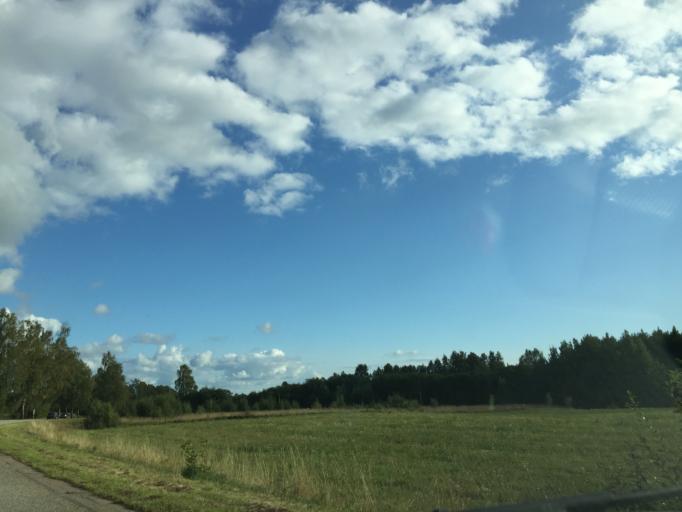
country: LV
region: Krimulda
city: Ragana
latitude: 57.2725
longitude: 24.6657
